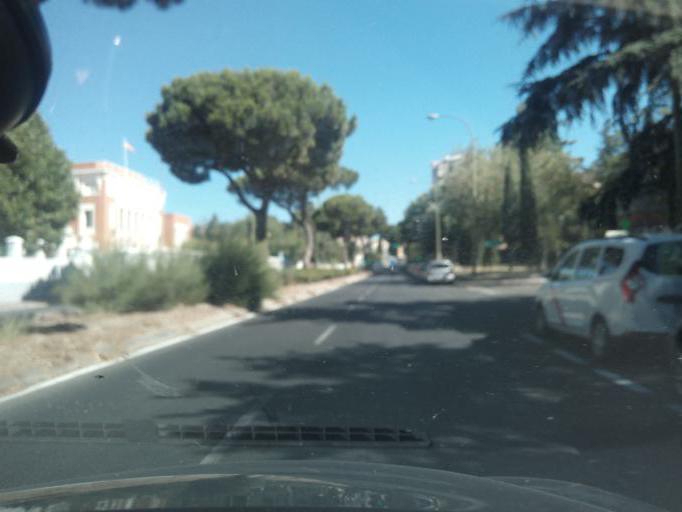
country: ES
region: Madrid
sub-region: Provincia de Madrid
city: Pinar de Chamartin
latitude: 40.4722
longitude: -3.6674
